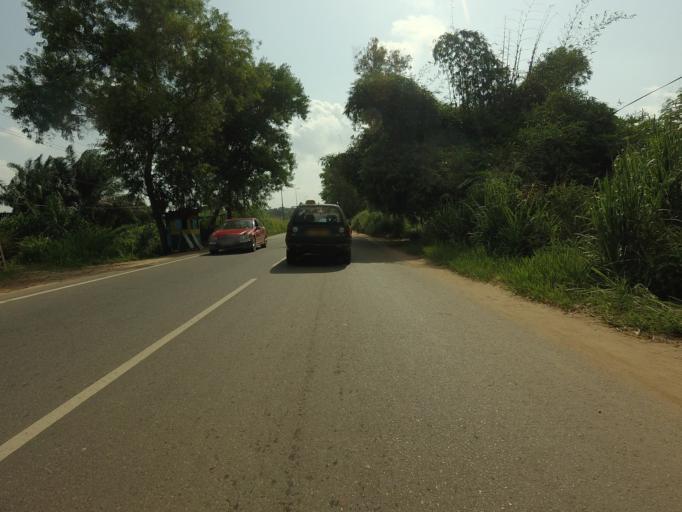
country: GH
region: Volta
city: Ho
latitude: 6.6025
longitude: 0.4905
